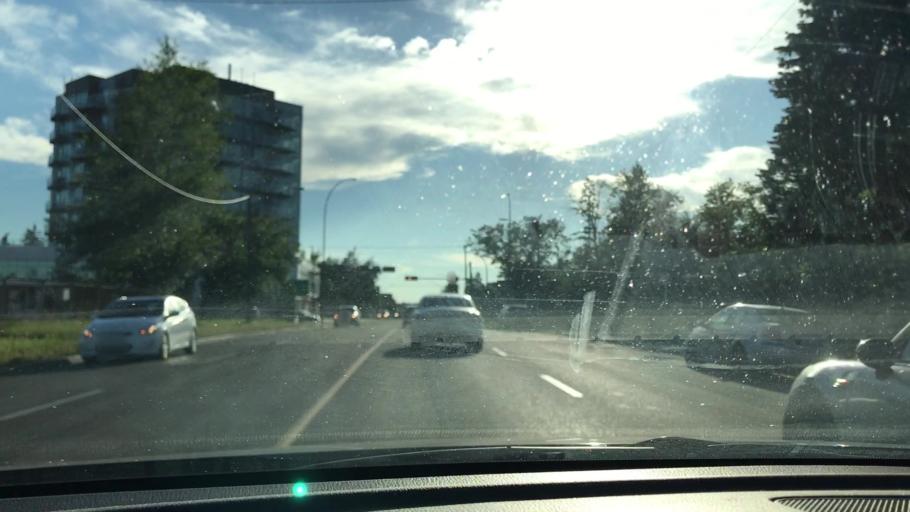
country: CA
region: Alberta
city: Calgary
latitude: 51.0378
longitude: -114.1165
